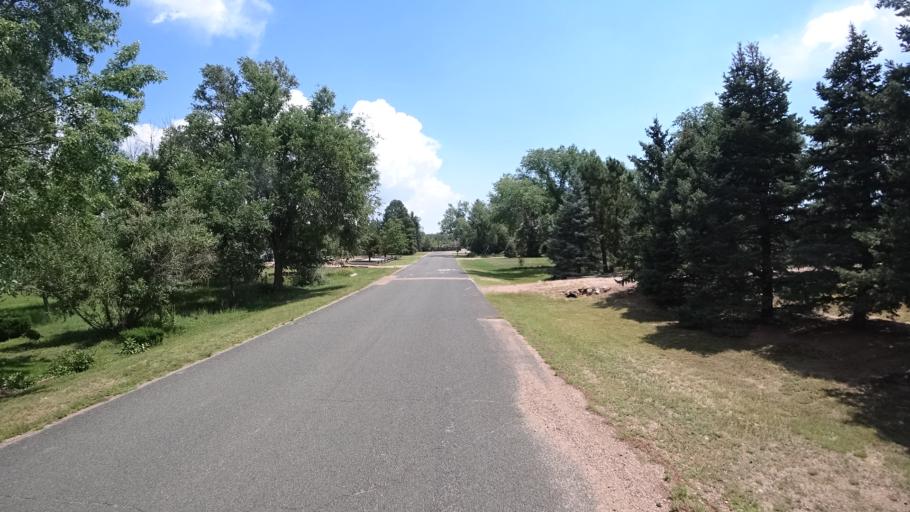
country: US
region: Colorado
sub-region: El Paso County
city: Air Force Academy
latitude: 38.9396
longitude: -104.8017
